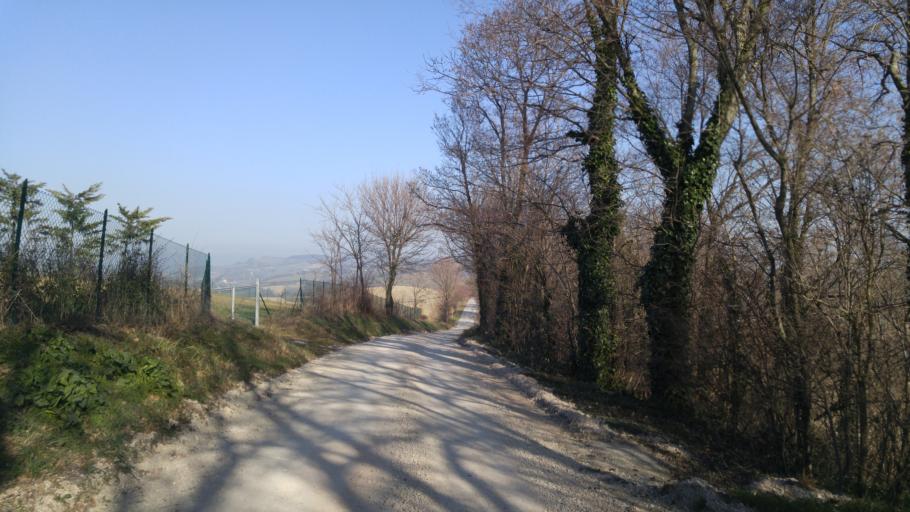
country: IT
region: The Marches
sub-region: Provincia di Pesaro e Urbino
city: Cuccurano
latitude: 43.8092
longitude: 12.9236
